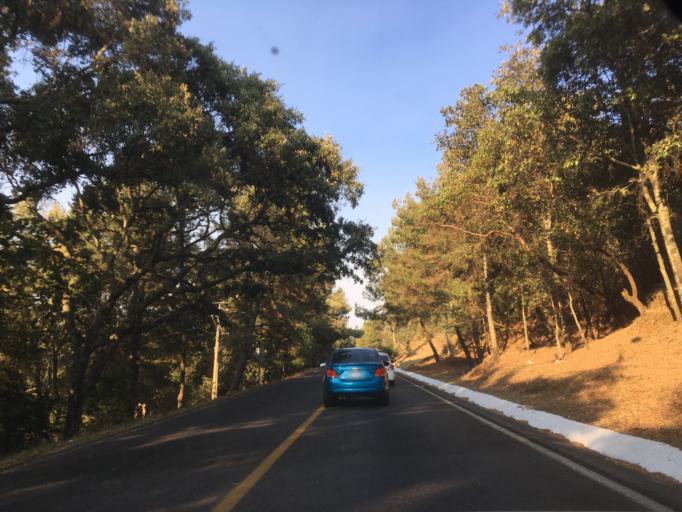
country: MX
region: Michoacan
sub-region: Morelia
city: Iratzio
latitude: 19.6290
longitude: -101.4541
